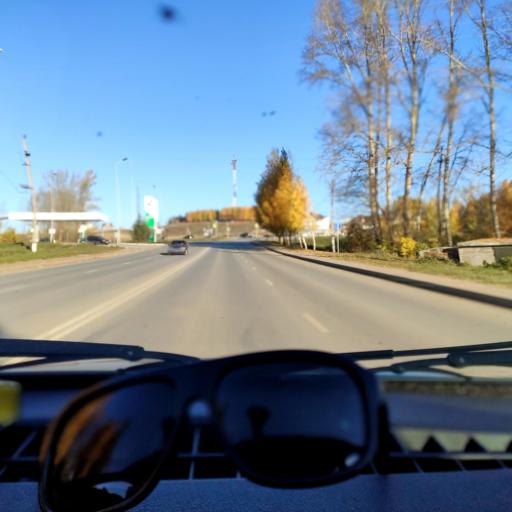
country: RU
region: Bashkortostan
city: Blagoveshchensk
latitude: 55.0547
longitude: 55.9493
